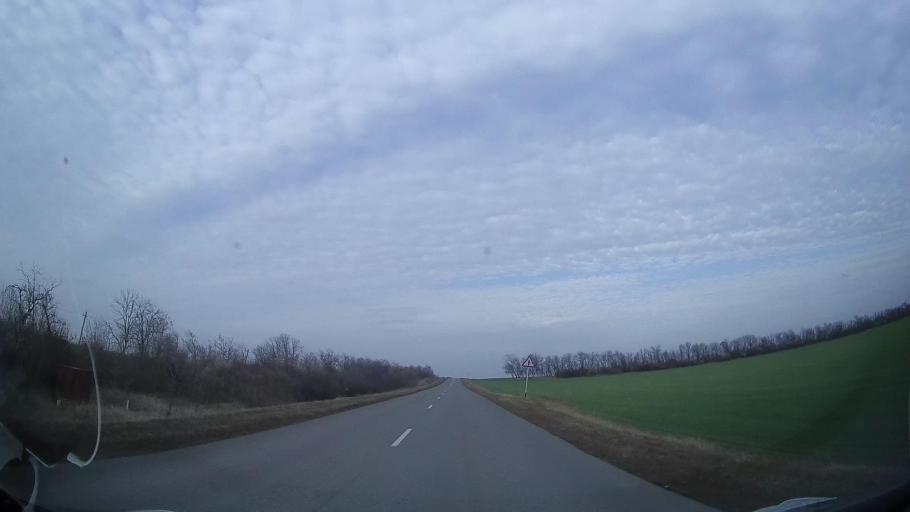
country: RU
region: Rostov
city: Zernograd
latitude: 46.9100
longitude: 40.3389
